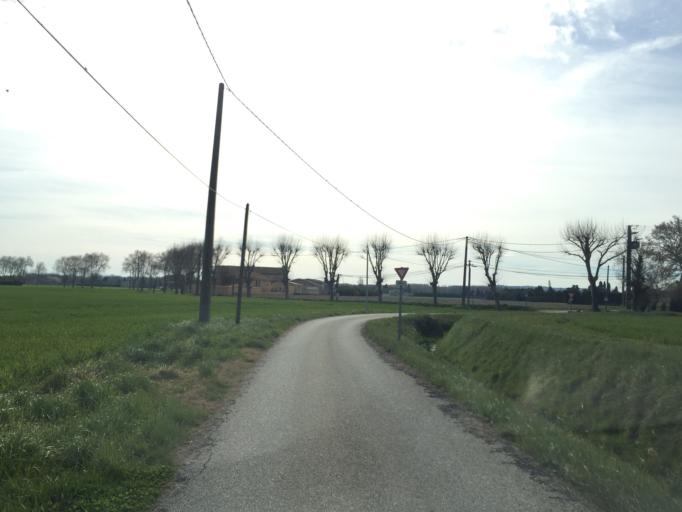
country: FR
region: Provence-Alpes-Cote d'Azur
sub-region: Departement du Vaucluse
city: Caderousse
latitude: 44.1109
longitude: 4.7440
